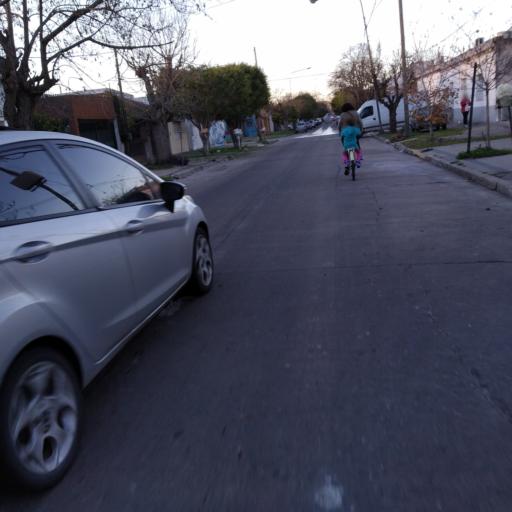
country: AR
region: Buenos Aires
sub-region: Partido de La Plata
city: La Plata
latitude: -34.9468
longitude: -57.9513
